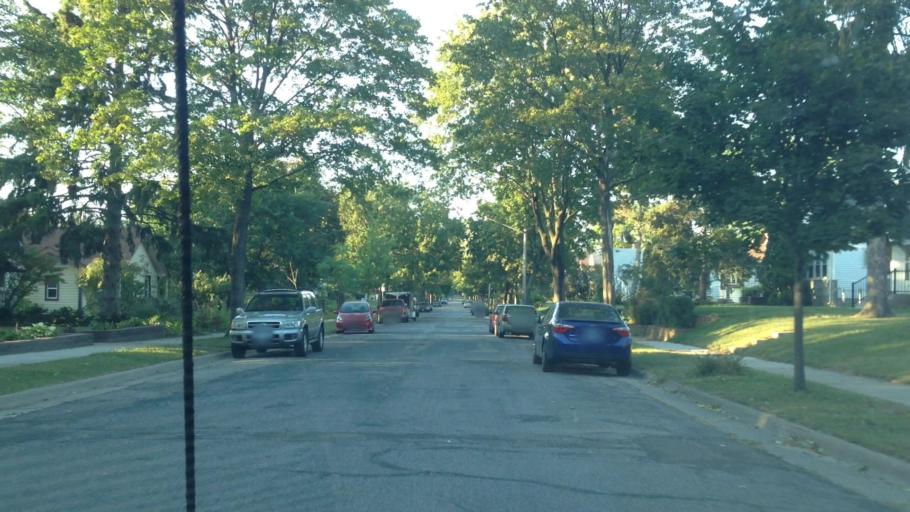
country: US
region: Minnesota
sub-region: Hennepin County
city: Richfield
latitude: 44.8999
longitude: -93.2115
